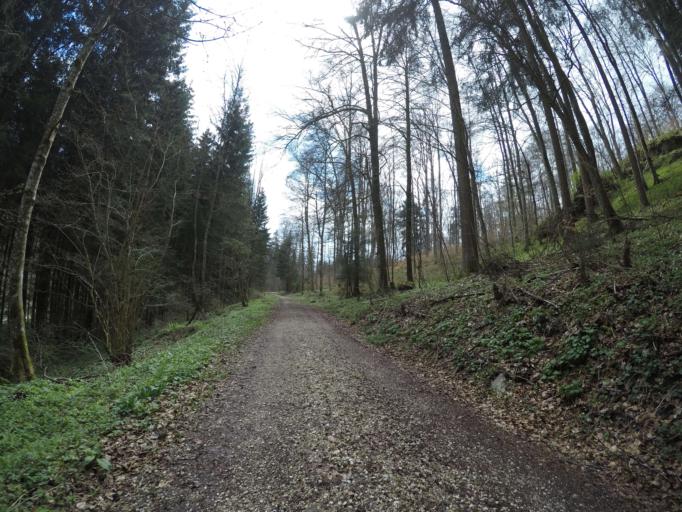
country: DE
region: Baden-Wuerttemberg
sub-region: Tuebingen Region
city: Berghulen
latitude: 48.4910
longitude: 9.7986
